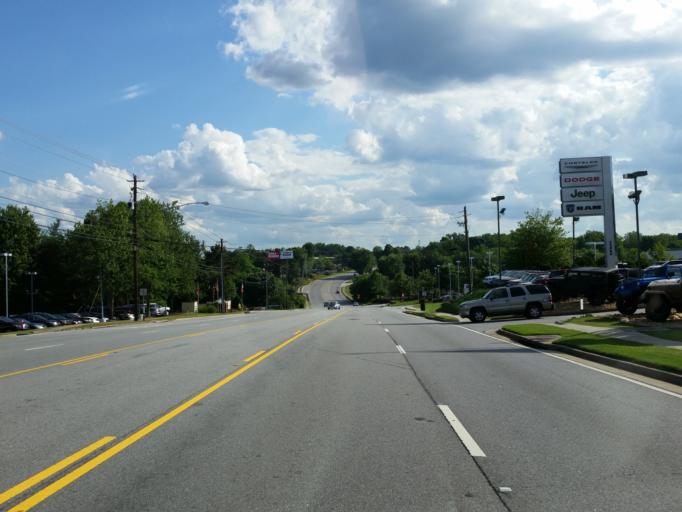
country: US
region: Georgia
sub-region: Fulton County
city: Alpharetta
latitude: 34.0592
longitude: -84.3261
